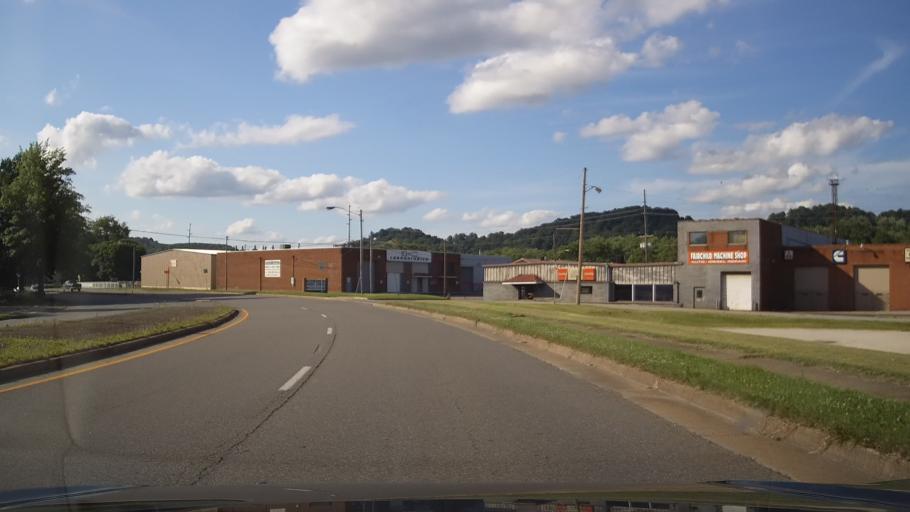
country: US
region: Kentucky
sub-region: Boyd County
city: Ashland
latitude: 38.4679
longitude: -82.6196
